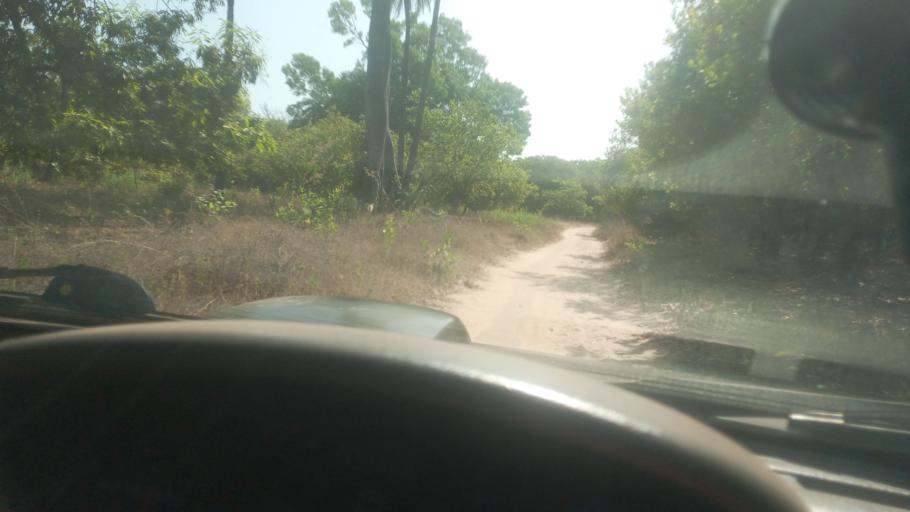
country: GW
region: Oio
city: Farim
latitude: 12.4478
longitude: -15.4303
